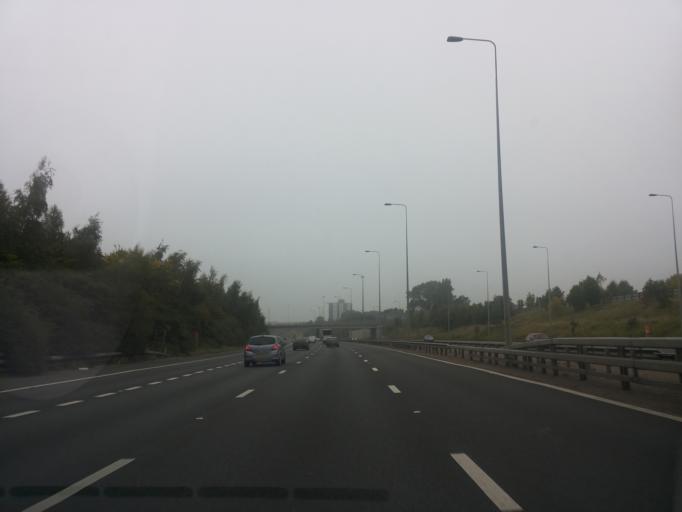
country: GB
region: England
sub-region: Manchester
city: Failsworth
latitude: 53.5136
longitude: -2.1363
